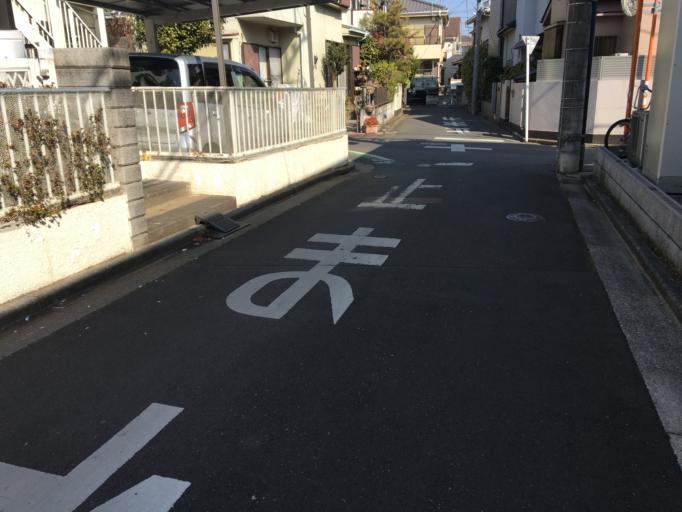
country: JP
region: Saitama
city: Oi
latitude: 35.8378
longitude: 139.5349
